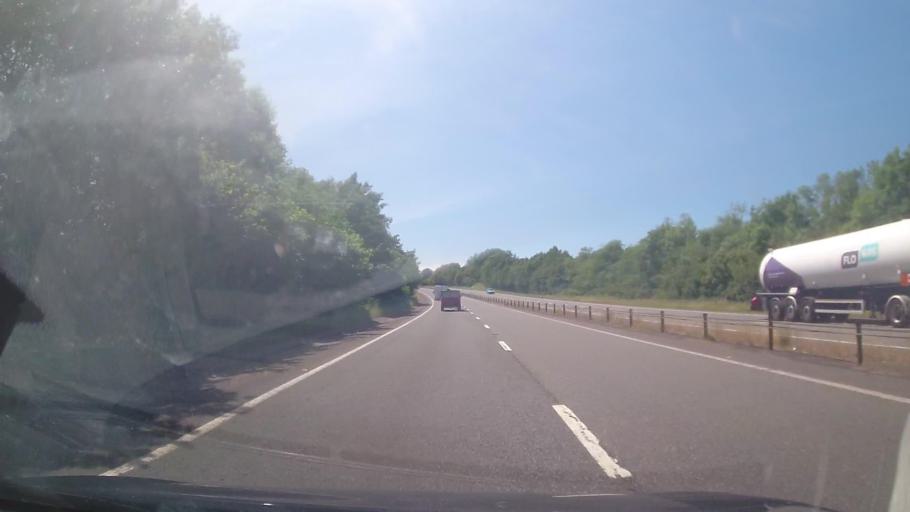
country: GB
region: England
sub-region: Devon
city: Ottery St Mary
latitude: 50.7822
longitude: -3.2581
